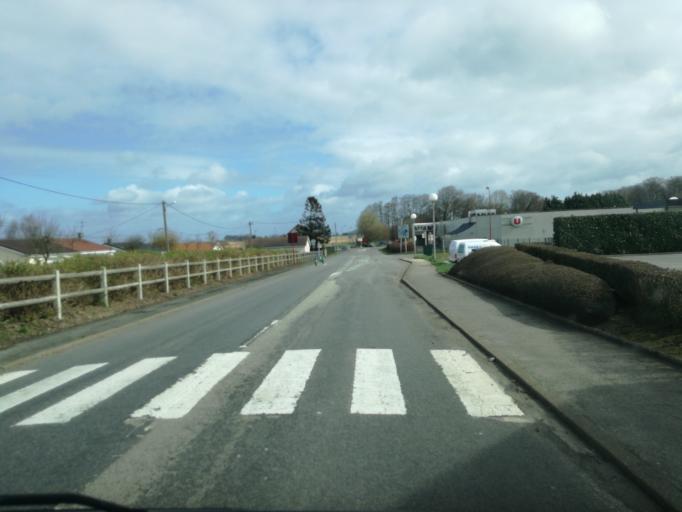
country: FR
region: Haute-Normandie
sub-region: Departement de la Seine-Maritime
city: Fauville-en-Caux
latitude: 49.6530
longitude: 0.5986
